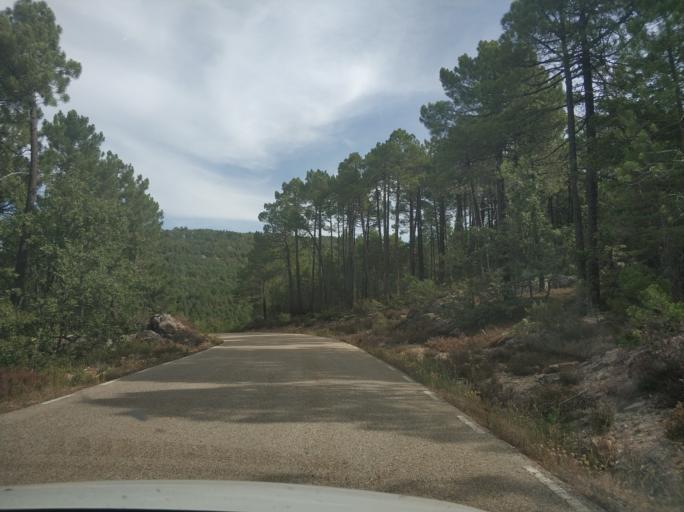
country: ES
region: Castille and Leon
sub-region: Provincia de Soria
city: Duruelo de la Sierra
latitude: 41.8978
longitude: -2.9422
